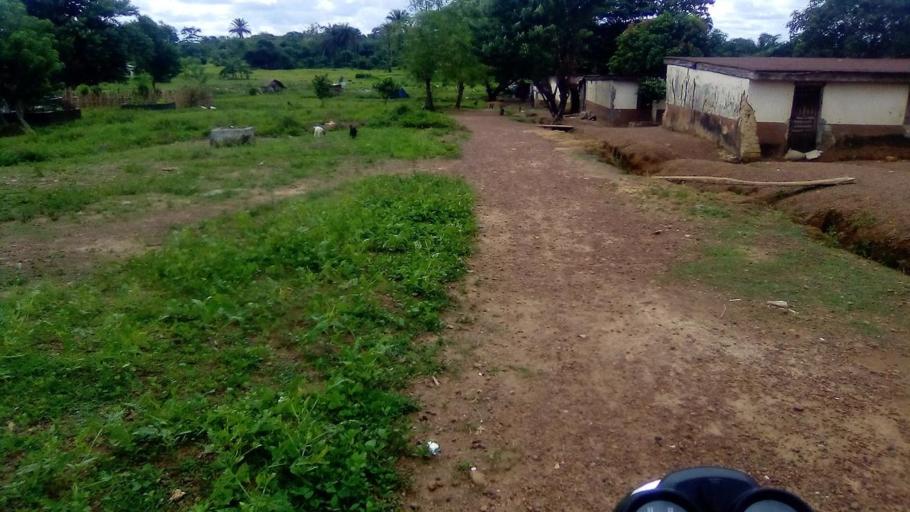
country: SL
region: Southern Province
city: Pujehun
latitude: 7.3708
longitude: -11.7257
